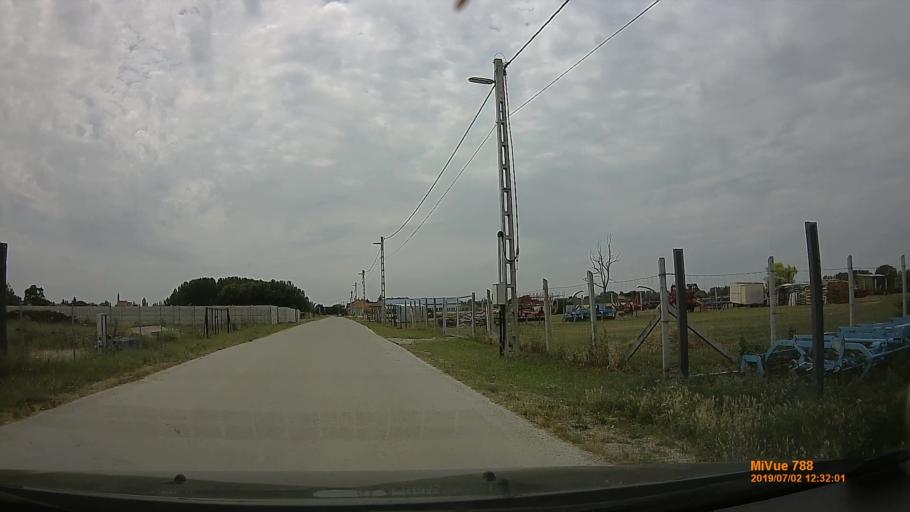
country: HU
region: Gyor-Moson-Sopron
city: Janossomorja
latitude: 47.8549
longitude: 17.1707
